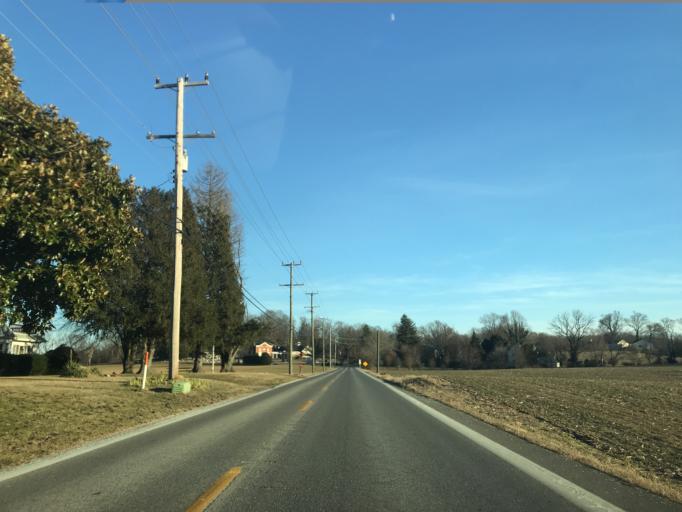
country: US
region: Maryland
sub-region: Anne Arundel County
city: Deale
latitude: 38.8339
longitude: -76.6207
